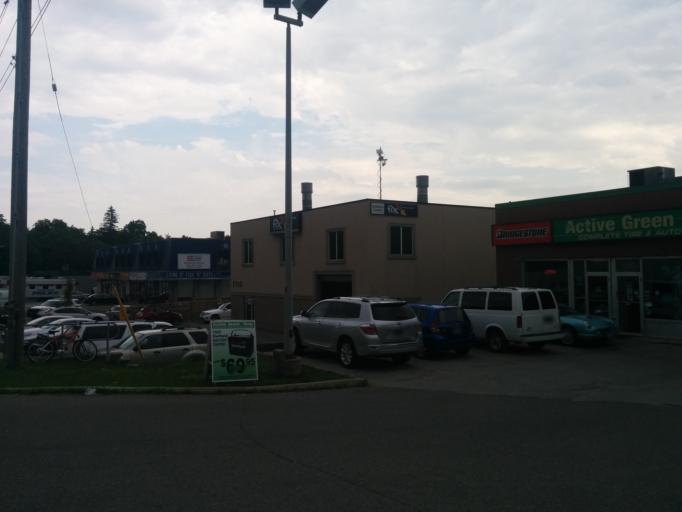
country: CA
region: Ontario
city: Vaughan
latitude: 43.7799
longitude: -79.5887
